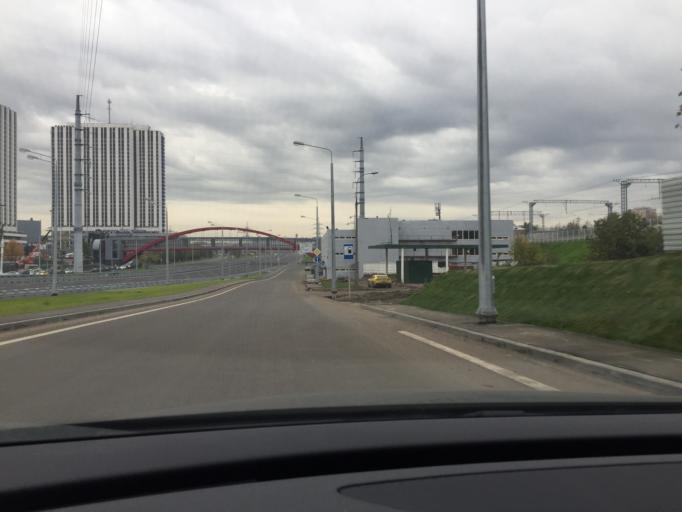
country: RU
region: Moskovskaya
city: Bogorodskoye
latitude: 55.7952
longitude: 37.7463
